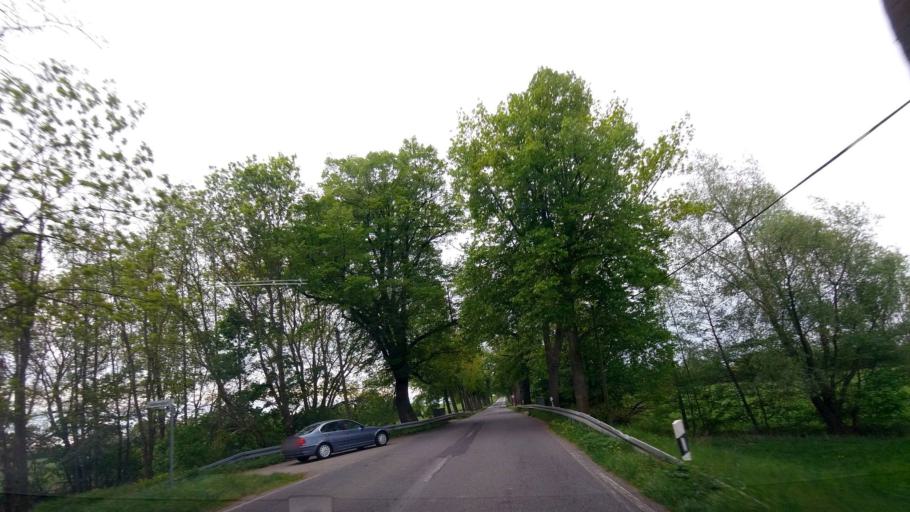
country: DE
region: Brandenburg
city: Dahme
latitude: 51.8876
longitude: 13.4185
